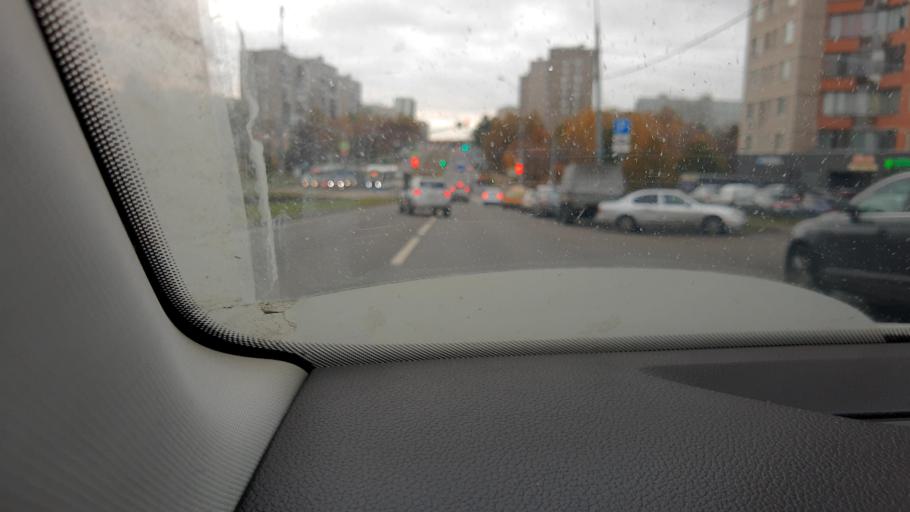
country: RU
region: Moscow
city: Chertanovo Yuzhnoye
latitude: 55.6060
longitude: 37.5830
